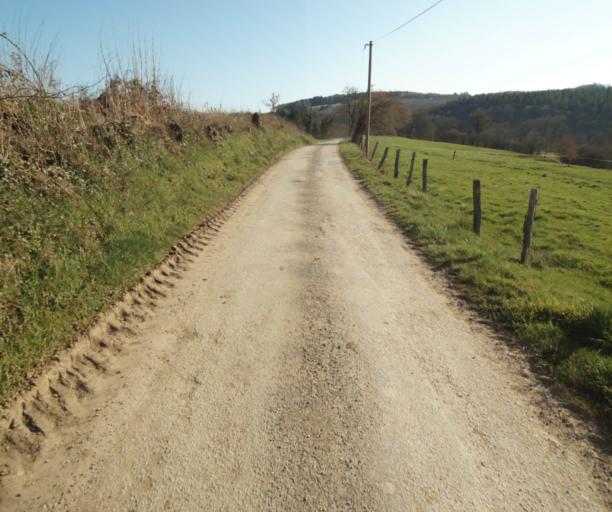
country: FR
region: Limousin
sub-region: Departement de la Correze
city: Chamboulive
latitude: 45.4961
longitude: 1.7288
